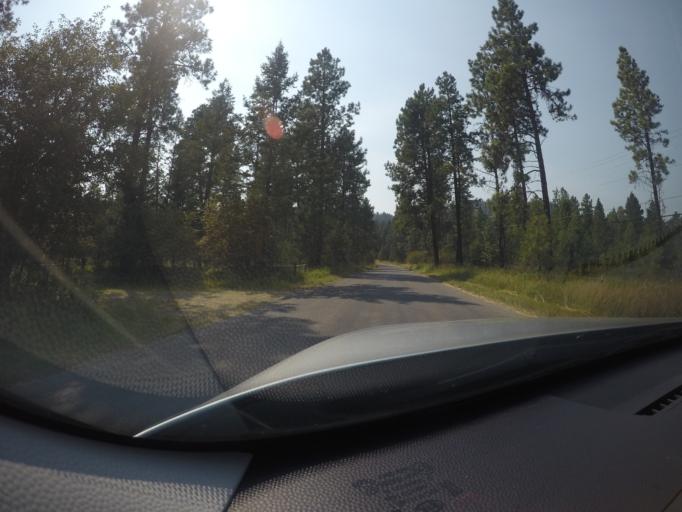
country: US
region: Montana
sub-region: Lake County
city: Polson
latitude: 47.7719
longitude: -114.1462
